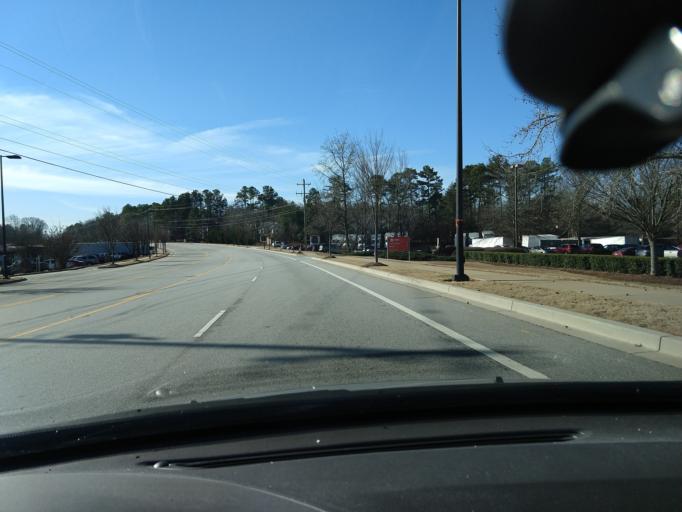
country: US
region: South Carolina
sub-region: Greenville County
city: Mauldin
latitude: 34.8004
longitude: -82.3457
